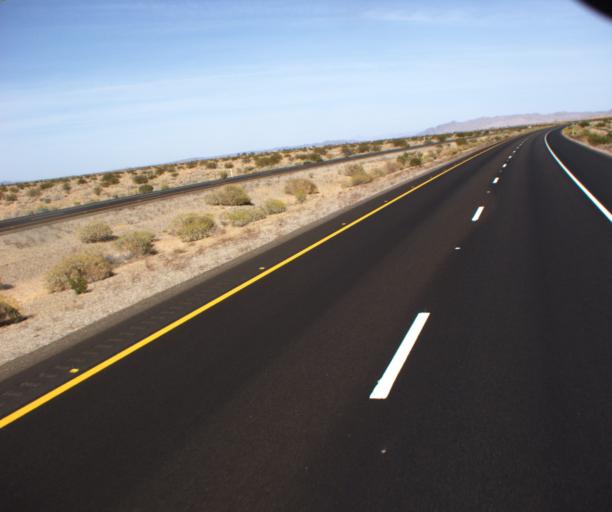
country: US
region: Arizona
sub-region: Yuma County
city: Fortuna Foothills
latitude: 32.6022
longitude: -114.5381
